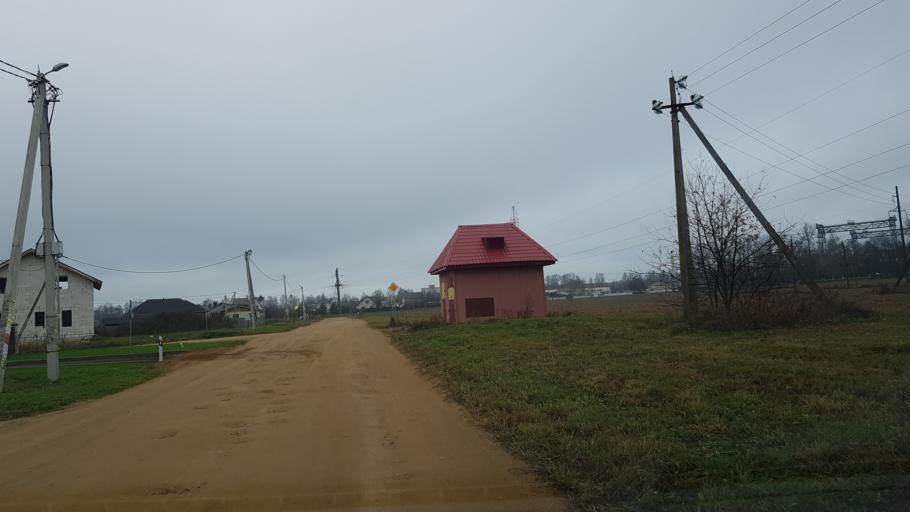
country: BY
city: Fanipol
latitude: 53.7327
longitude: 27.3269
